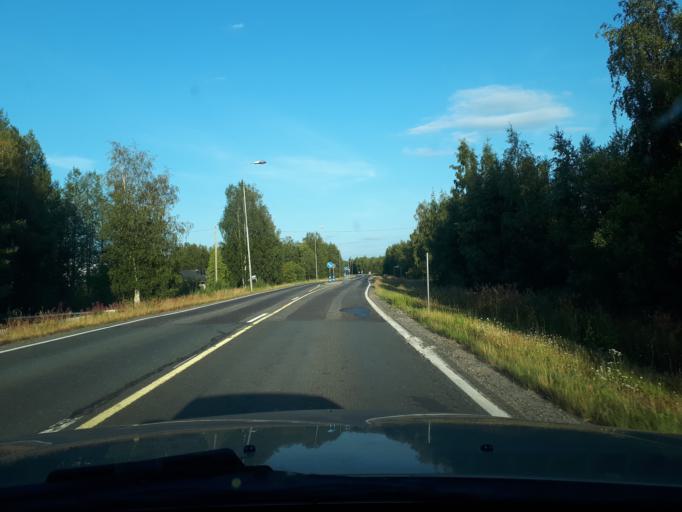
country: FI
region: Northern Ostrobothnia
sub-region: Oulu
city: Oulunsalo
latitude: 64.9745
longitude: 25.3211
